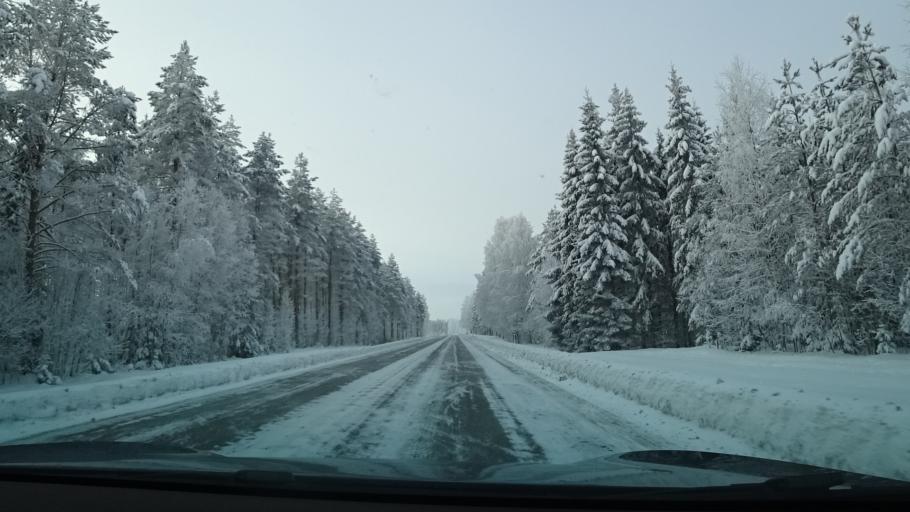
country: FI
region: South Karelia
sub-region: Imatra
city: Saari
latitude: 61.7808
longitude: 29.7059
